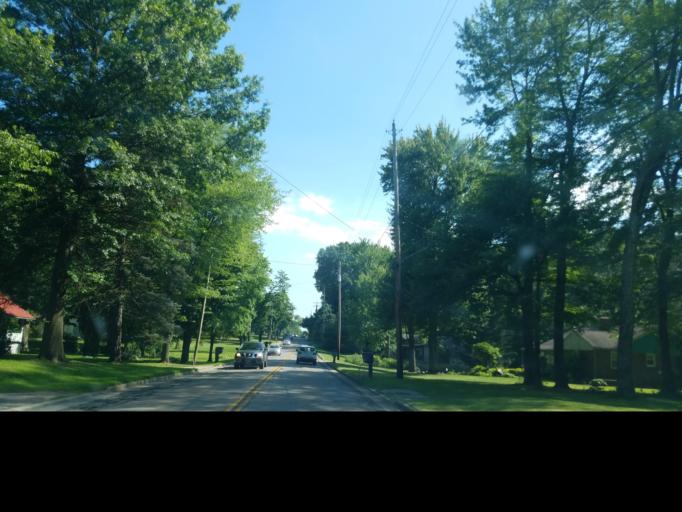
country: US
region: Ohio
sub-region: Portage County
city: Ravenna
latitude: 41.1664
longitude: -81.2719
